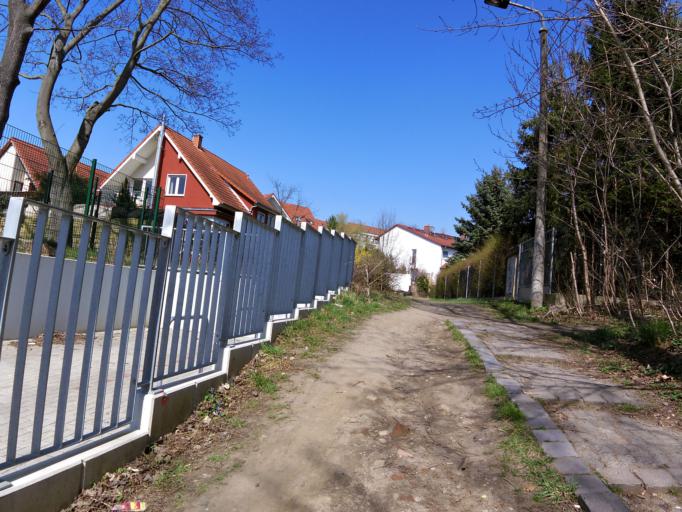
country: DE
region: Saxony
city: Leipzig
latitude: 51.3736
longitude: 12.3196
